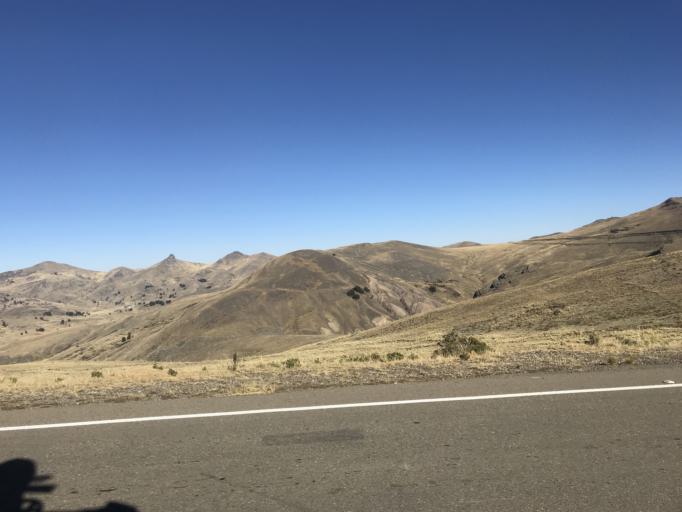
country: PE
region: Puno
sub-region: Yunguyo
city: Yunguyo
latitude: -16.1601
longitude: -68.9910
